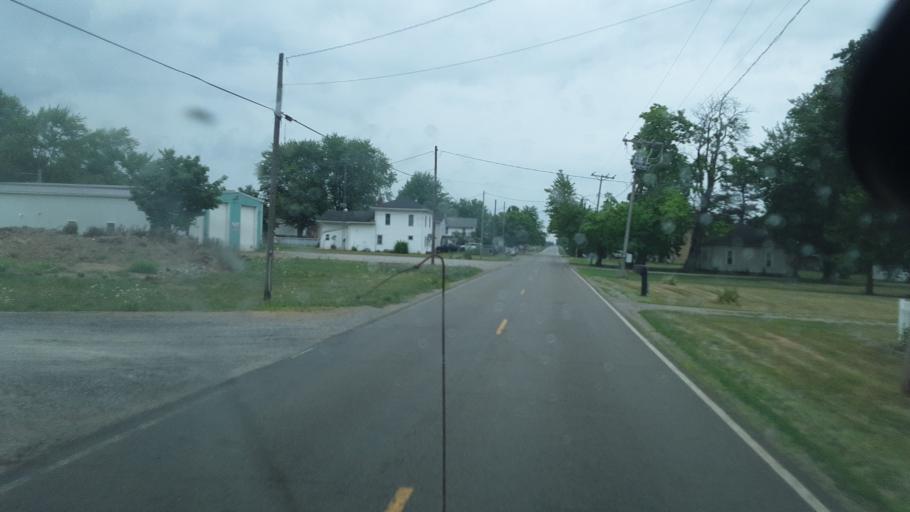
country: US
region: Ohio
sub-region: Williams County
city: Bryan
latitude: 41.3816
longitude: -84.6311
